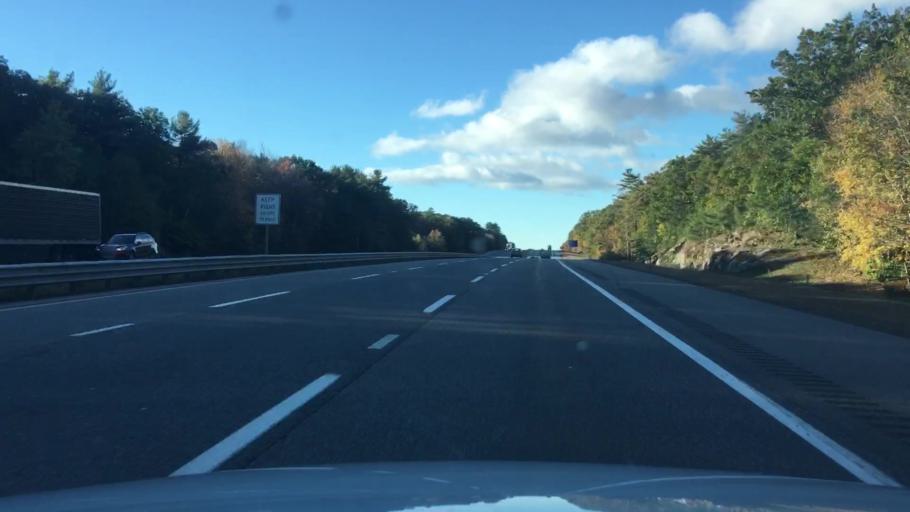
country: US
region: Maine
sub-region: York County
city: Cape Neddick
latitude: 43.1864
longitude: -70.6466
